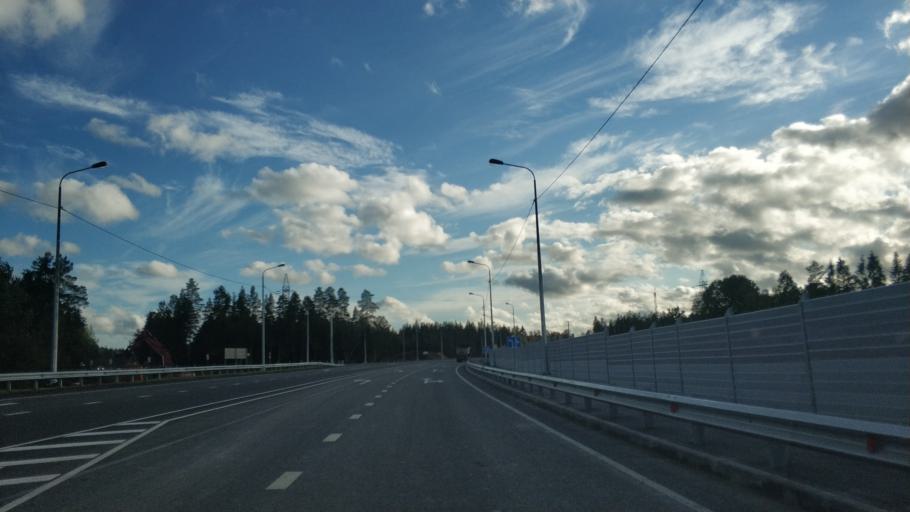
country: RU
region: Leningrad
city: Priozersk
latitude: 60.8490
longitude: 30.1464
